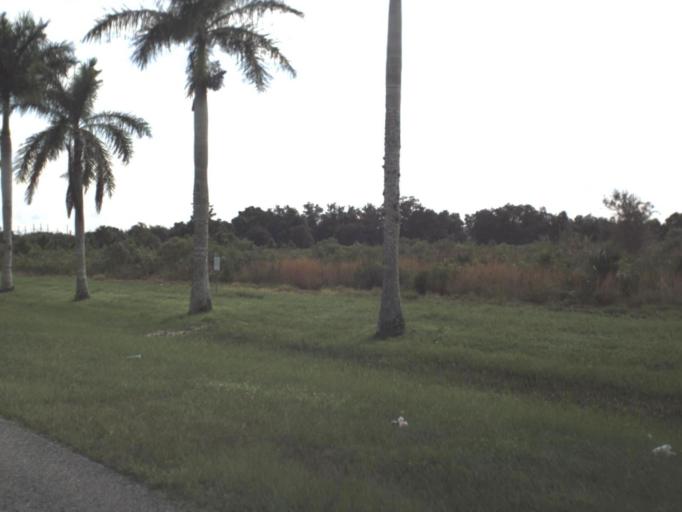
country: US
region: Florida
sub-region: Lee County
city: Tice
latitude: 26.6913
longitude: -81.7857
